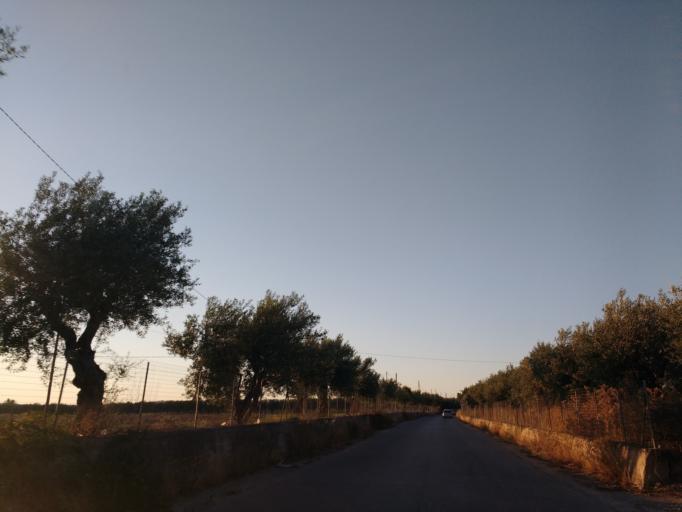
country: IT
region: Sicily
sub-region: Ragusa
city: Ispica
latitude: 36.7517
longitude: 14.9229
